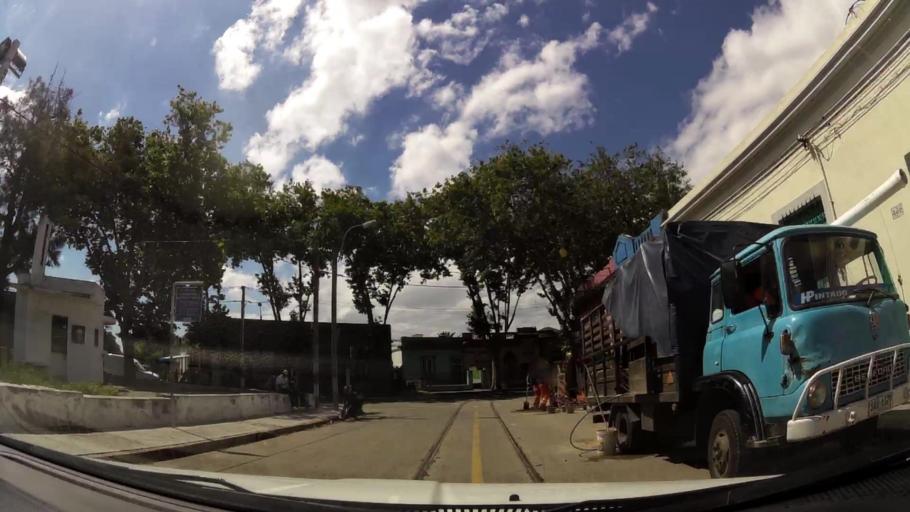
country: UY
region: Montevideo
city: Montevideo
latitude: -34.8716
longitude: -56.2134
